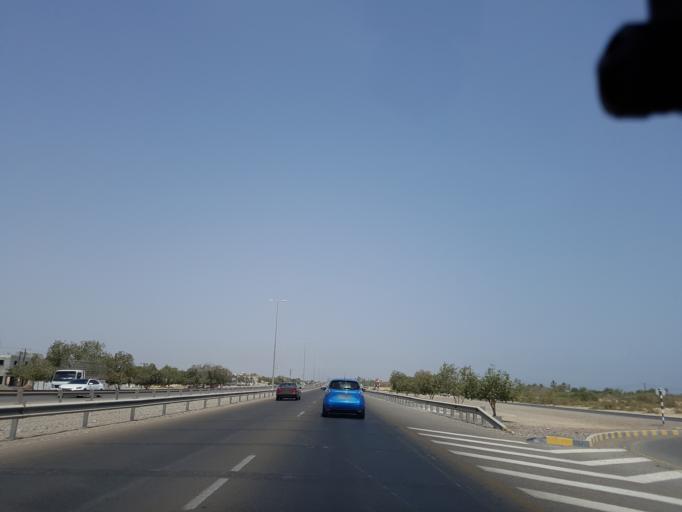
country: OM
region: Al Batinah
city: Saham
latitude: 24.2155
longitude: 56.8427
